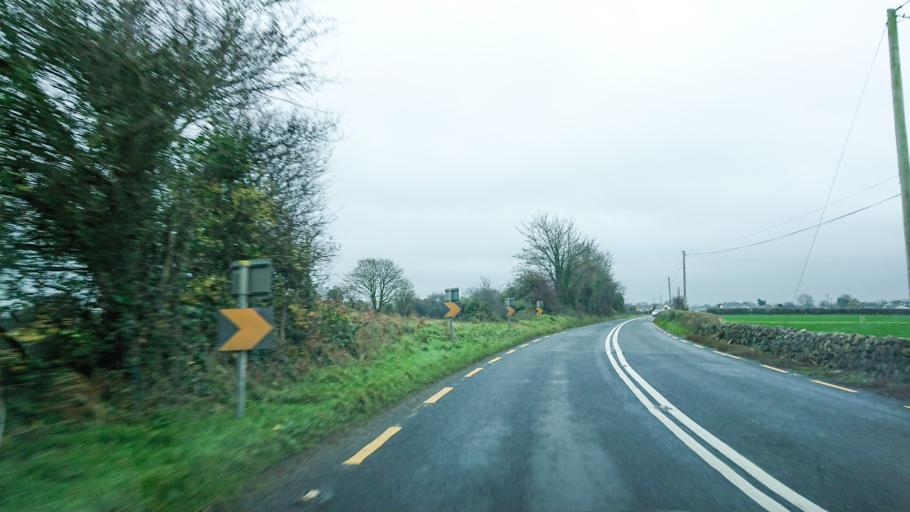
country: IE
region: Leinster
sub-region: Kilkenny
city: Mooncoin
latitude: 52.3032
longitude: -7.2742
